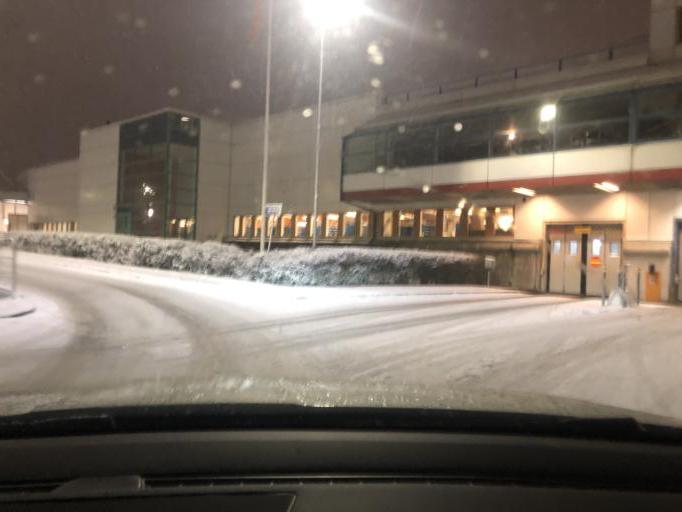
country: SE
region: Stockholm
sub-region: Stockholms Kommun
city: Arsta
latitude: 59.2879
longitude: 18.0534
